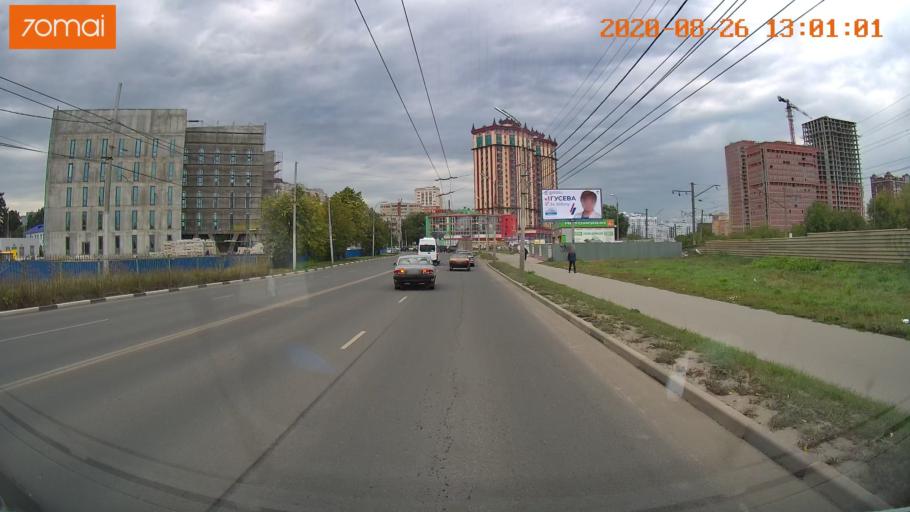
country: RU
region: Rjazan
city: Ryazan'
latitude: 54.6174
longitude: 39.7372
